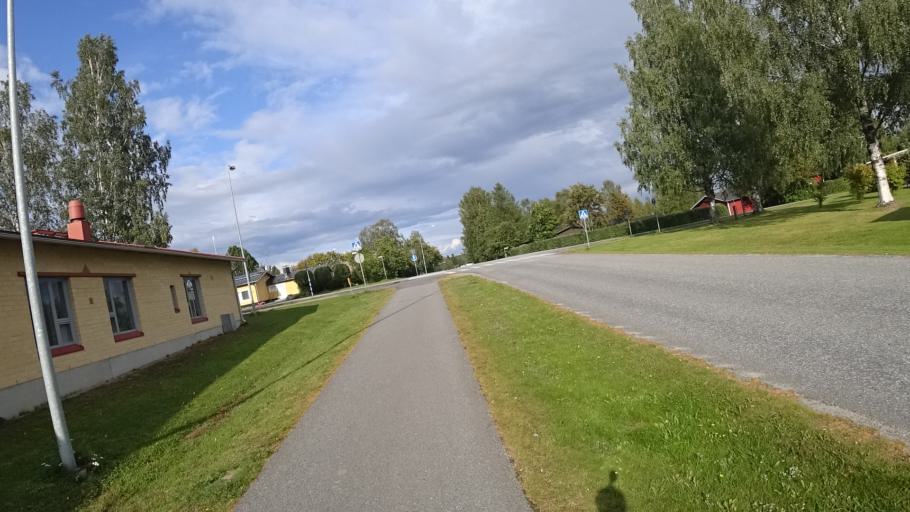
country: FI
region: North Karelia
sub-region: Joensuu
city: Ilomantsi
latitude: 62.6693
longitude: 30.9225
